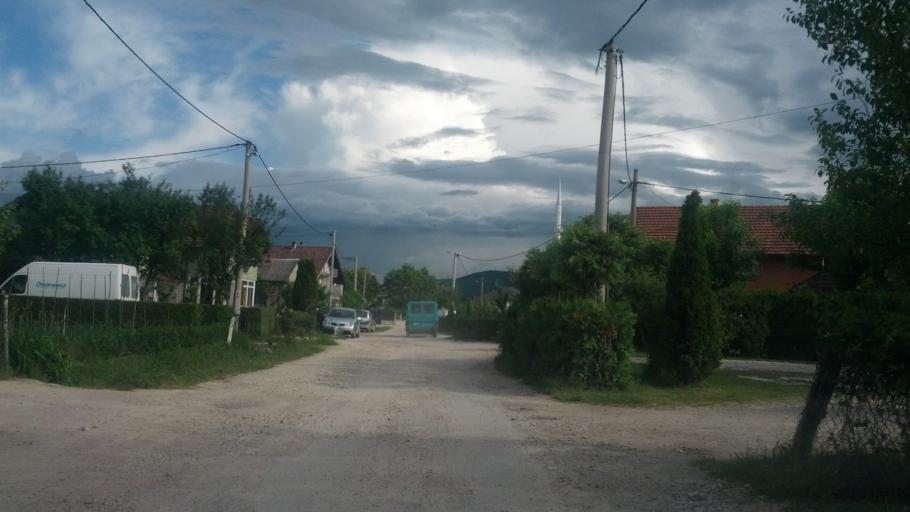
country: BA
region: Federation of Bosnia and Herzegovina
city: Bihac
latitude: 44.8387
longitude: 15.8759
